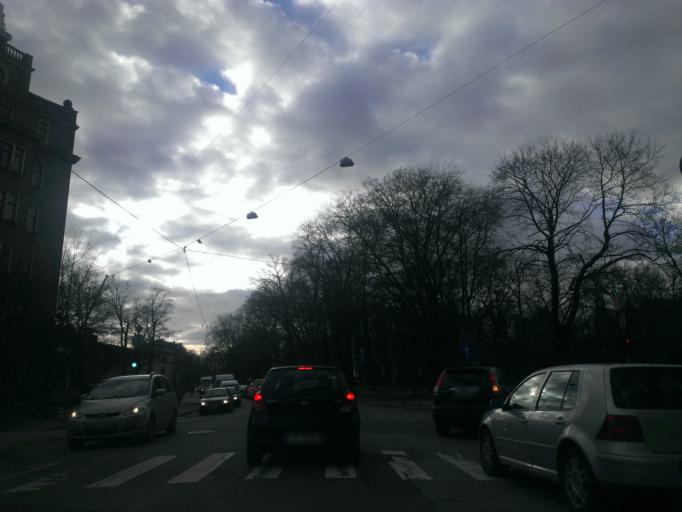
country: LV
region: Riga
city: Riga
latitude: 56.9628
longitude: 24.1040
